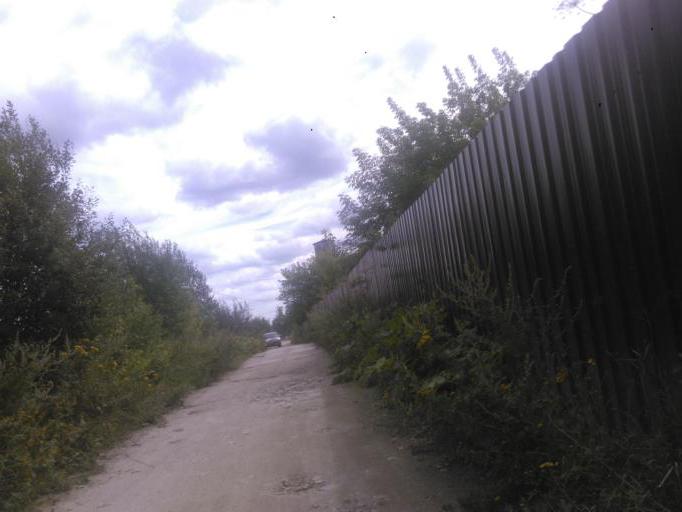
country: RU
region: Moskovskaya
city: Solnechnogorsk
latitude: 56.1464
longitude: 36.9182
